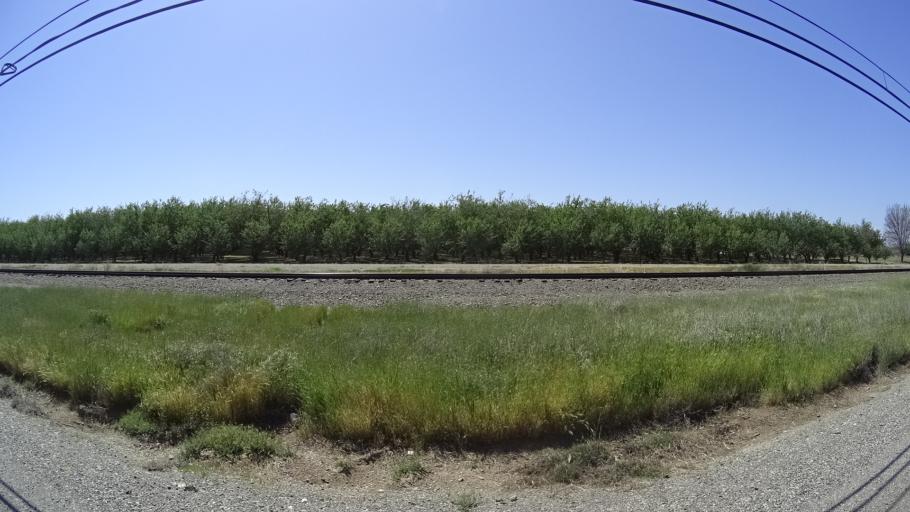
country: US
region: California
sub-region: Glenn County
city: Orland
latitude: 39.7689
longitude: -122.1831
